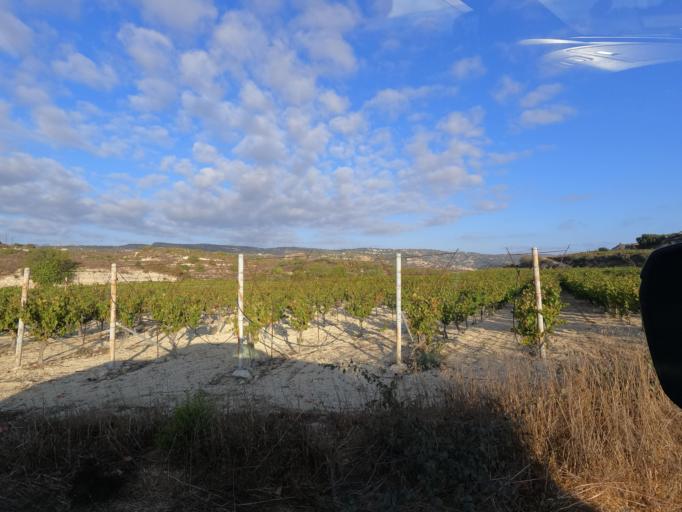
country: CY
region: Pafos
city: Mesogi
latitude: 34.8317
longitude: 32.5280
